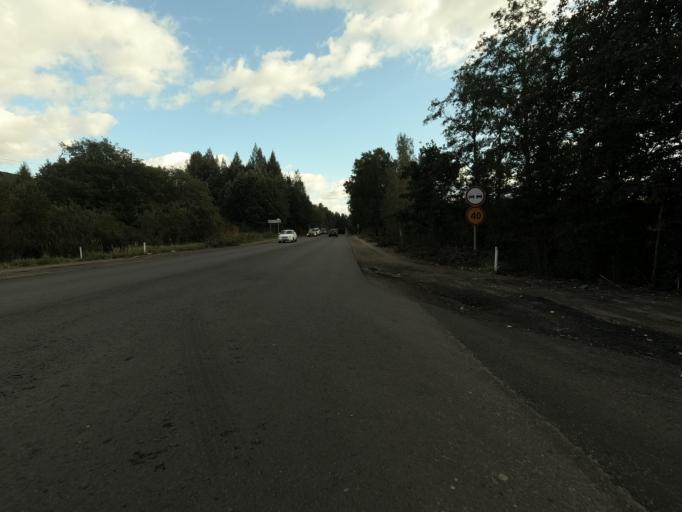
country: RU
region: Leningrad
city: Koltushi
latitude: 59.9698
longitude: 30.6545
